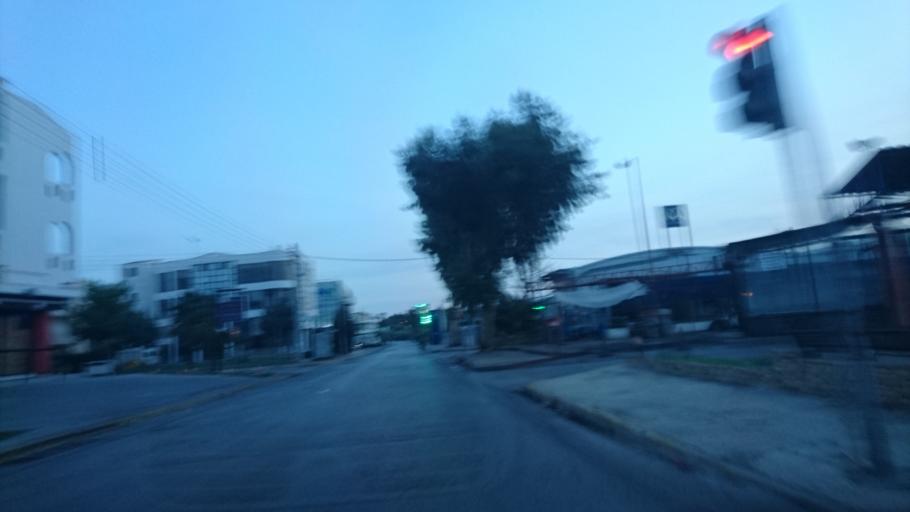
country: GR
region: Attica
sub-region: Nomarchia Athinas
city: Argyroupoli
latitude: 37.9068
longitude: 23.7381
